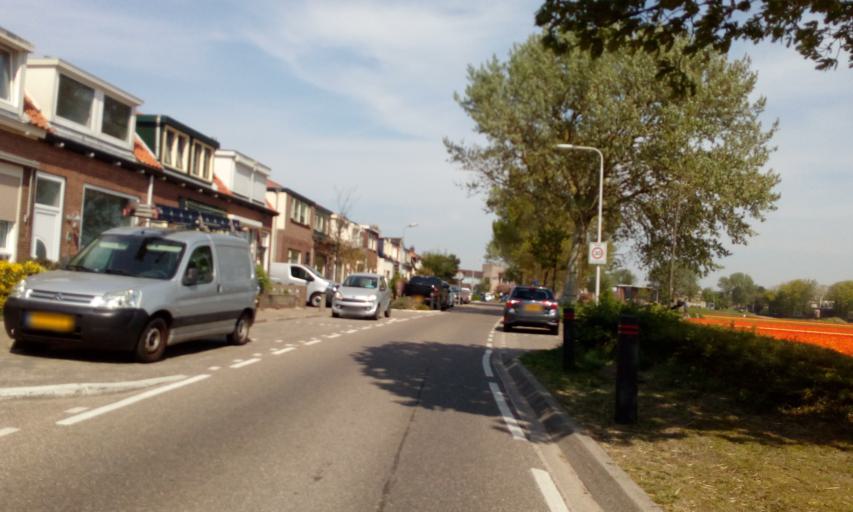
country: NL
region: South Holland
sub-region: Gemeente Hillegom
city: Hillegom
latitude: 52.2912
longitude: 4.5619
